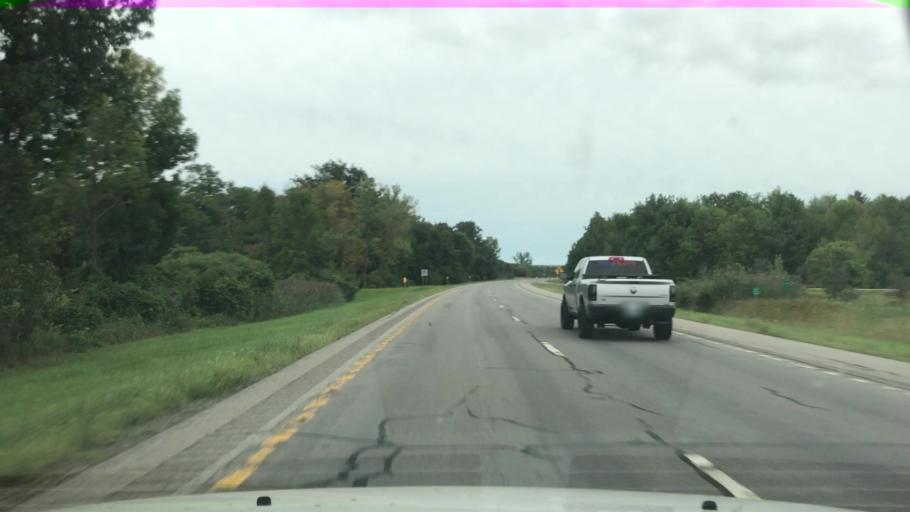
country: US
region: New York
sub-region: Erie County
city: Orchard Park
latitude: 42.7464
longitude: -78.7614
